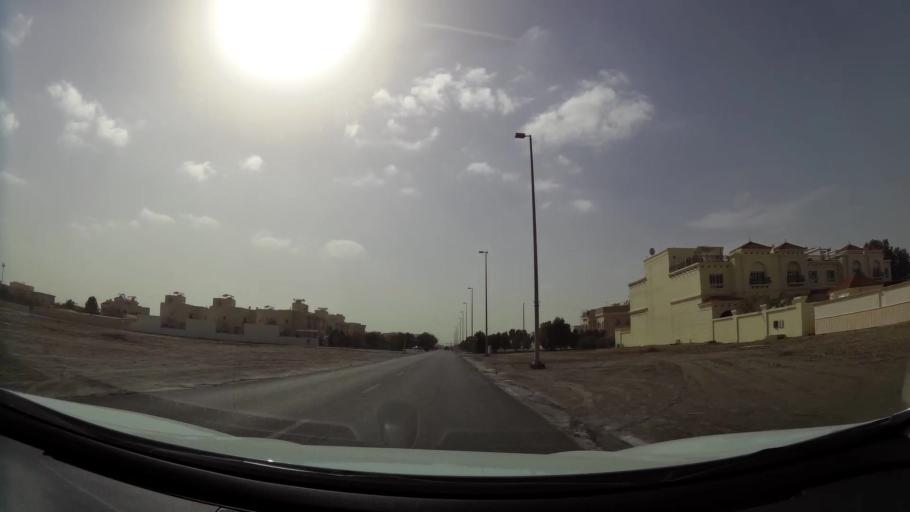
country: AE
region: Abu Dhabi
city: Abu Dhabi
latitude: 24.4262
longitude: 54.5711
